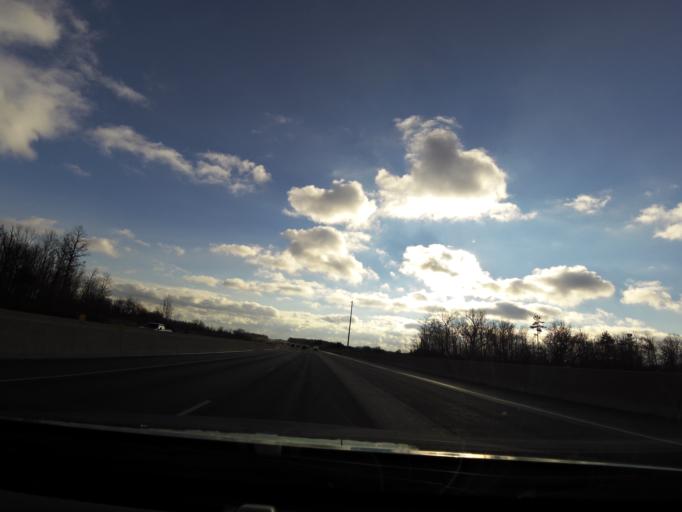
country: CA
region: Ontario
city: Burlington
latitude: 43.4663
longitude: -79.7848
